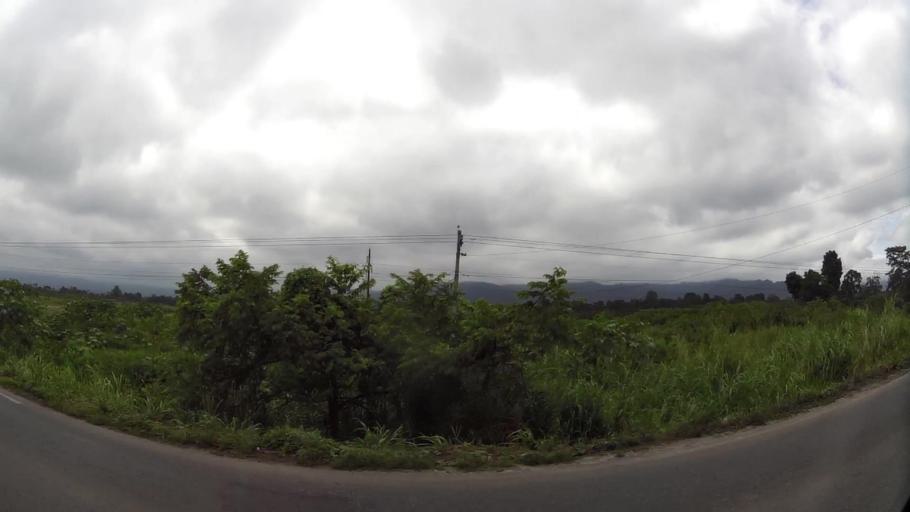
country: EC
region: Guayas
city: Naranjal
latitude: -2.6899
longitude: -79.6408
